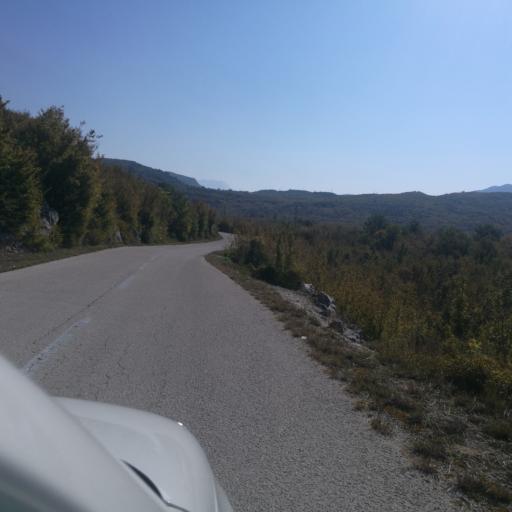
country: HR
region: Splitsko-Dalmatinska
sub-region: Grad Omis
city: Omis
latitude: 43.5197
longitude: 16.7548
